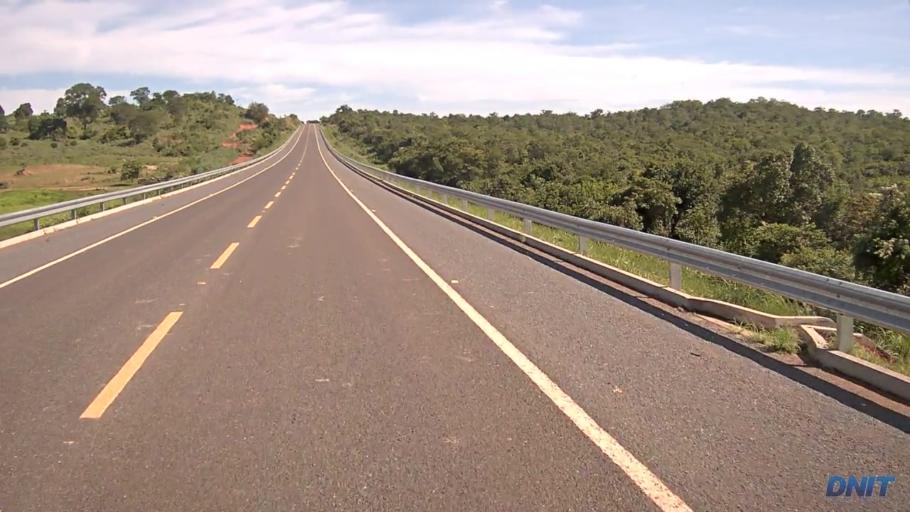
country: BR
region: Goias
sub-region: Sao Miguel Do Araguaia
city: Sao Miguel do Araguaia
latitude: -13.3346
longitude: -50.1539
